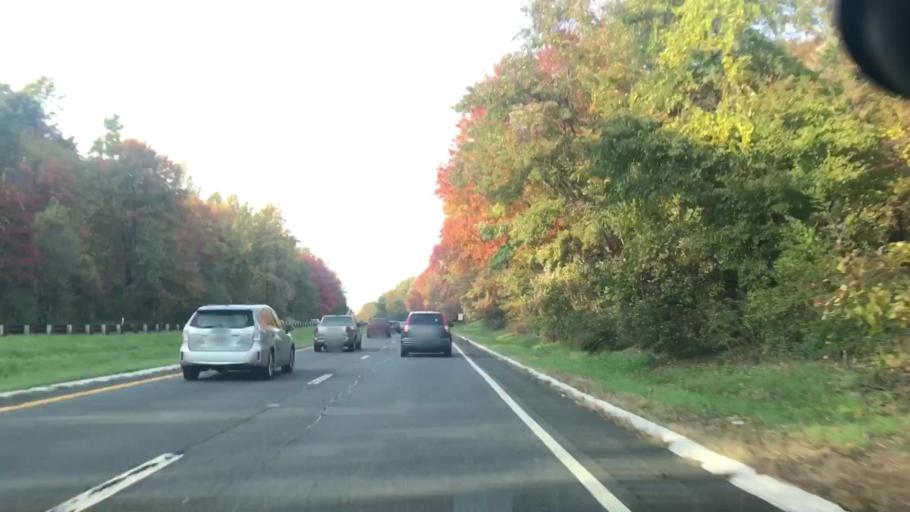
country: US
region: New York
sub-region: Rockland County
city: Blauvelt
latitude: 41.0714
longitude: -73.9810
